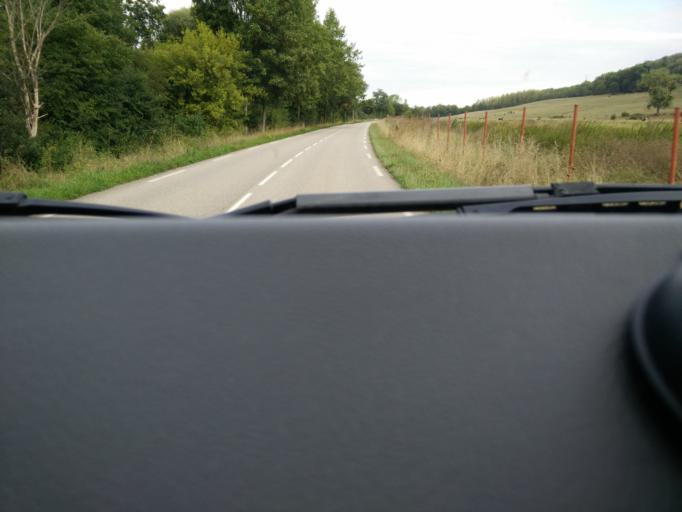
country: FR
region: Lorraine
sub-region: Departement de Meurthe-et-Moselle
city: Belleville
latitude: 48.8281
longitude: 6.0974
